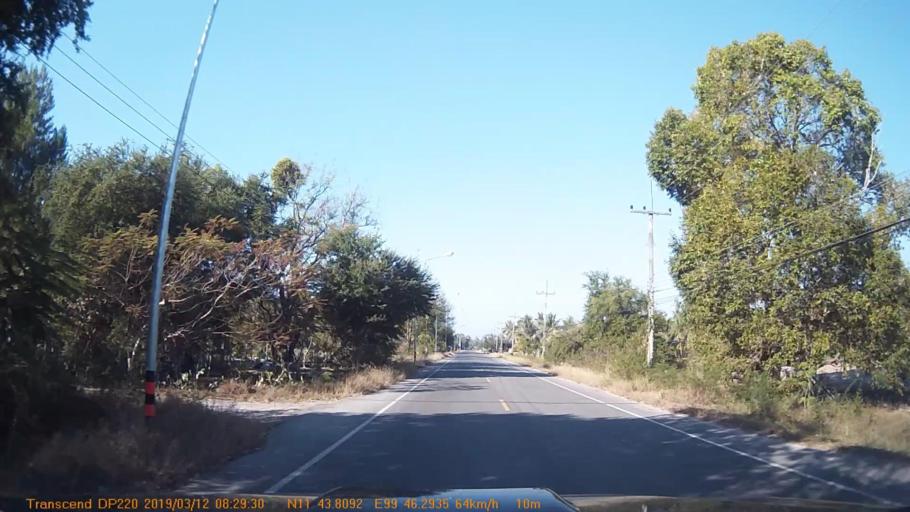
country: TH
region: Prachuap Khiri Khan
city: Prachuap Khiri Khan
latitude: 11.7300
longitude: 99.7714
